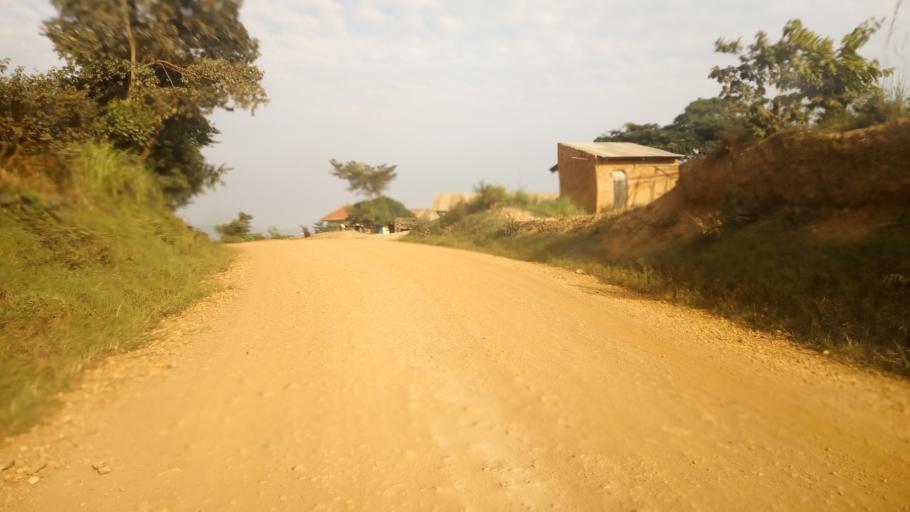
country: UG
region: Western Region
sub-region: Kanungu District
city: Ntungamo
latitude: -0.8346
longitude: 29.6801
